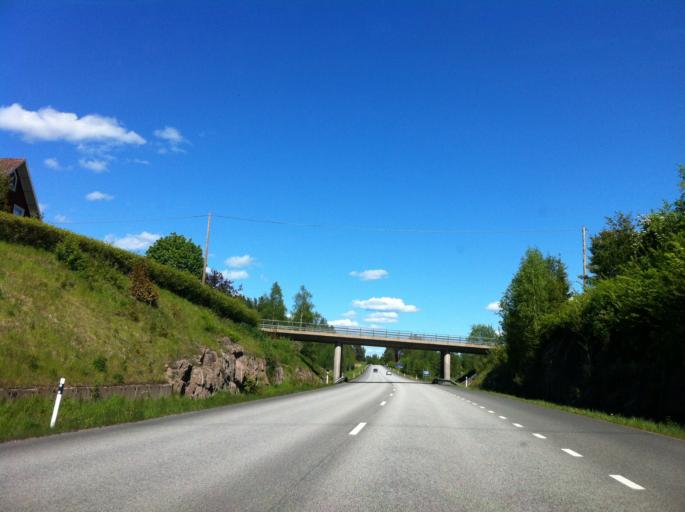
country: SE
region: Dalarna
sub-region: Rattviks Kommun
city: Vikarbyn
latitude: 60.9048
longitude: 14.9830
